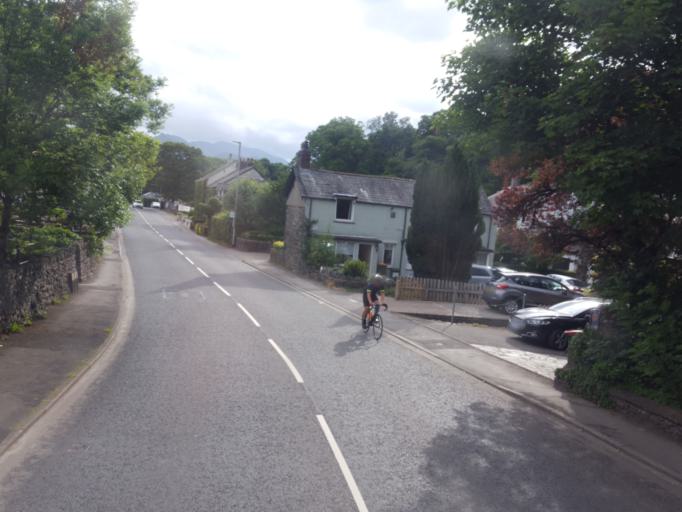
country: GB
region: England
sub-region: Cumbria
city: Keswick
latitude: 54.6049
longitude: -3.1224
